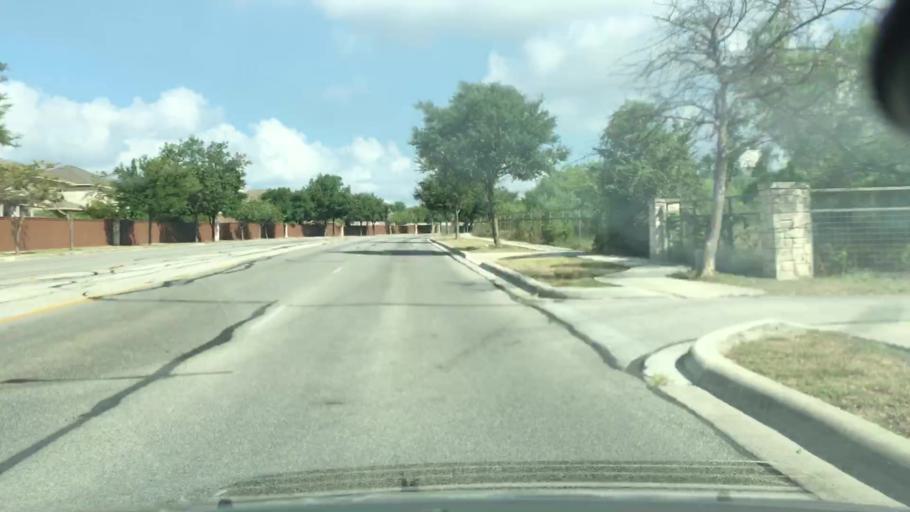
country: US
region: Texas
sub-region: Guadalupe County
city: Cibolo
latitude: 29.5800
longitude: -98.2457
